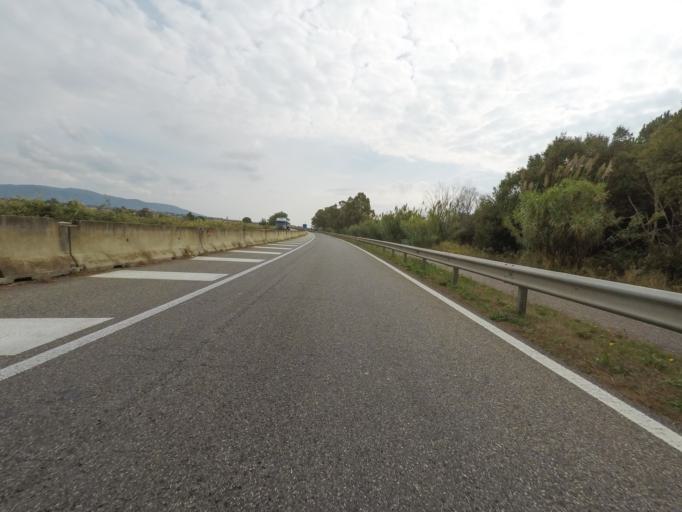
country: IT
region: Tuscany
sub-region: Provincia di Grosseto
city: Albinia
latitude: 42.5123
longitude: 11.1953
